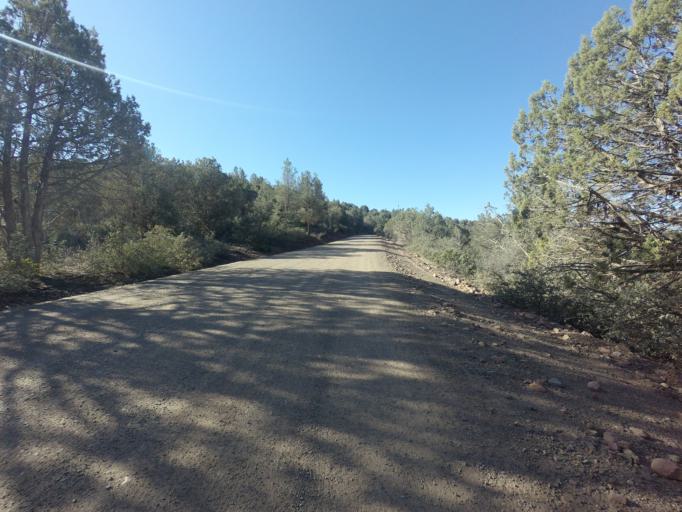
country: US
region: Arizona
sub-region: Gila County
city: Payson
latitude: 34.3003
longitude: -111.3516
